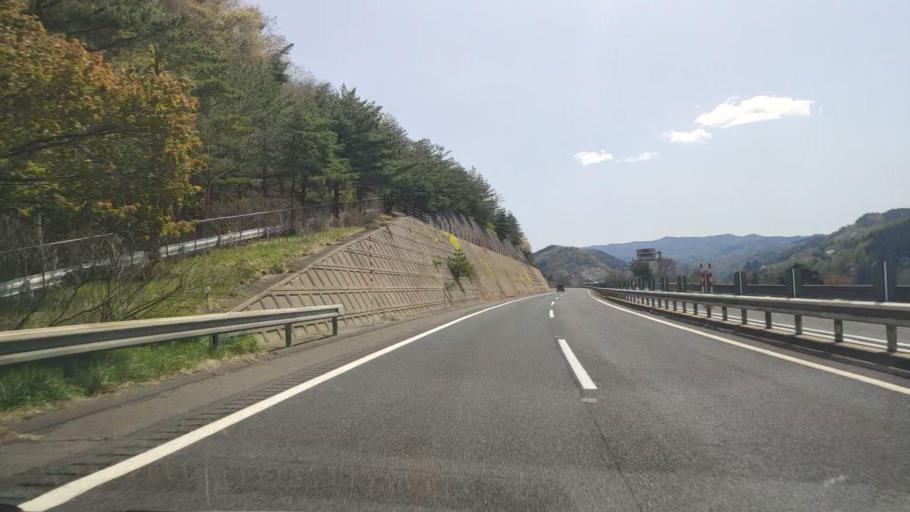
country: JP
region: Iwate
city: Ichinohe
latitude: 40.2311
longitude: 141.3125
